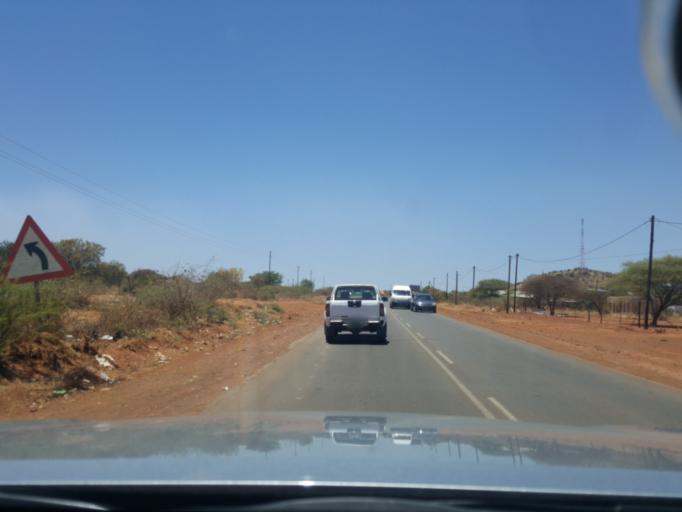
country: ZA
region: North-West
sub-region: Ngaka Modiri Molema District Municipality
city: Zeerust
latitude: -25.4703
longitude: 25.9746
